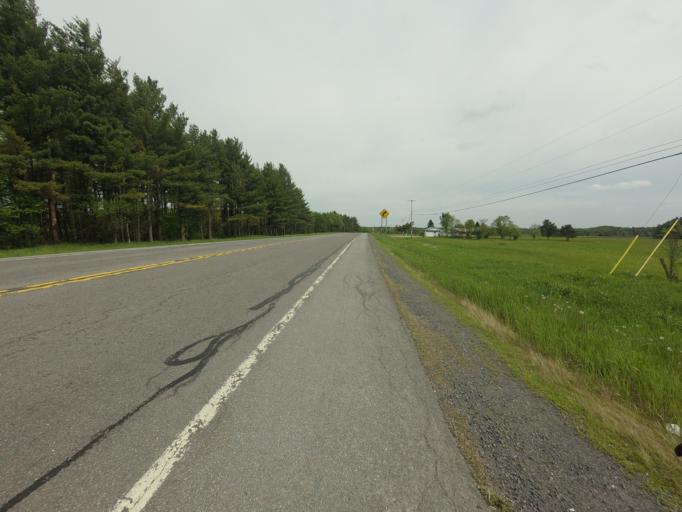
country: US
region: New York
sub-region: St. Lawrence County
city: Gouverneur
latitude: 44.3134
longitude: -75.2309
